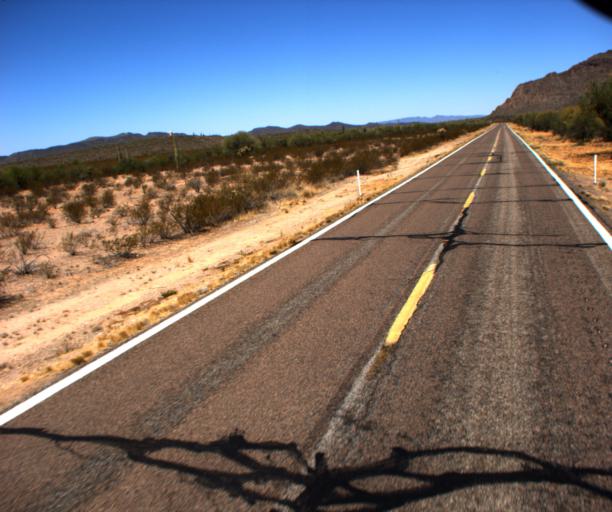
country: US
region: Arizona
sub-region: Pima County
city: Ajo
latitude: 32.2221
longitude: -112.6694
